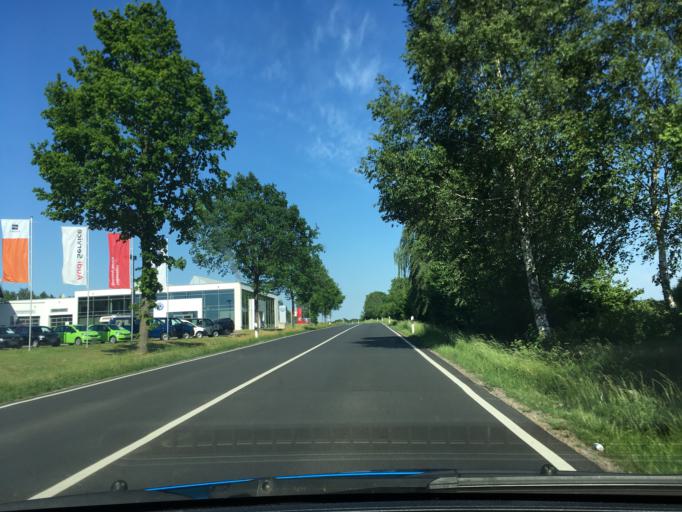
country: DE
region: Lower Saxony
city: Walsrode
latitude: 52.8605
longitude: 9.6146
